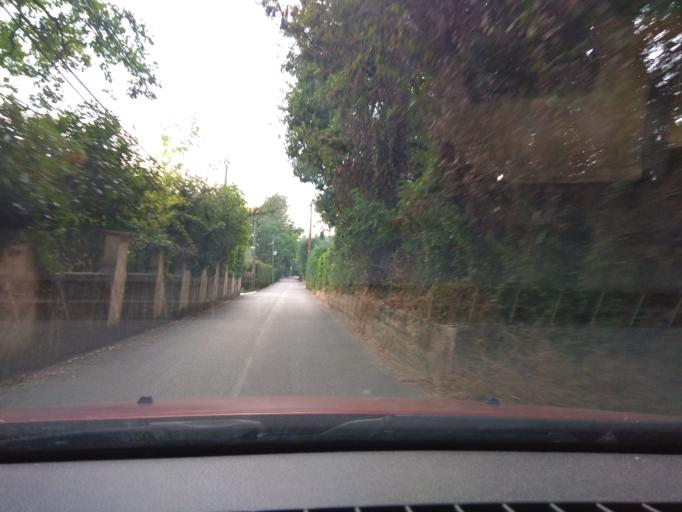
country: FR
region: Provence-Alpes-Cote d'Azur
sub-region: Departement des Alpes-Maritimes
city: Valbonne
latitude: 43.6438
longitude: 7.0271
